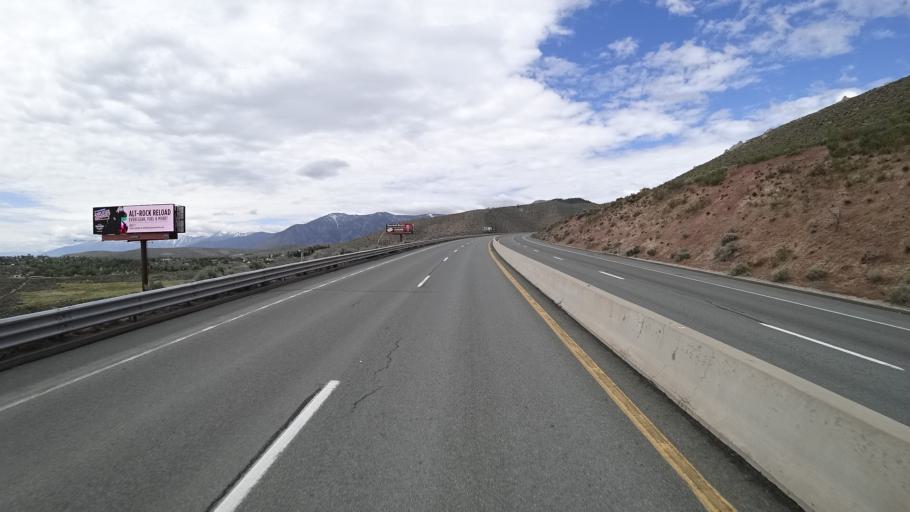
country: US
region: Nevada
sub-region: Douglas County
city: Indian Hills
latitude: 39.1142
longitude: -119.7844
